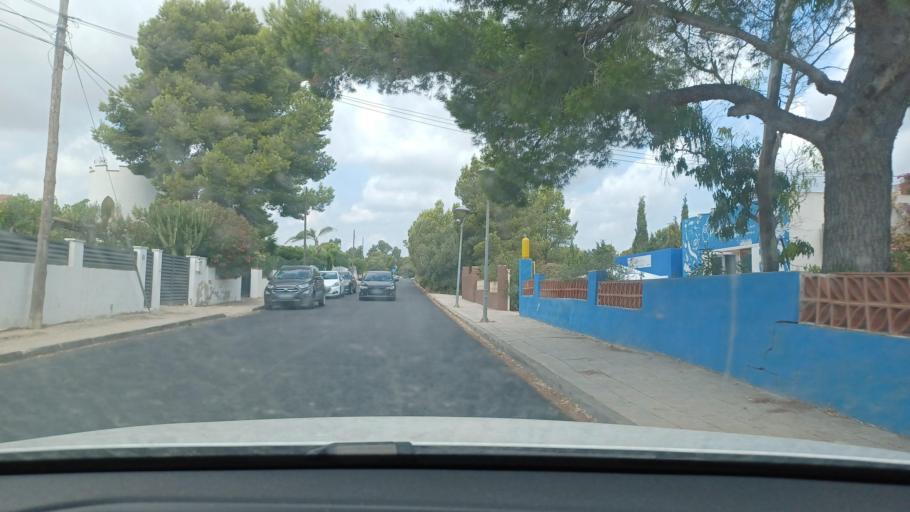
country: ES
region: Catalonia
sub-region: Provincia de Tarragona
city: l'Ametlla de Mar
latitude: 40.9075
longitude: 0.8121
